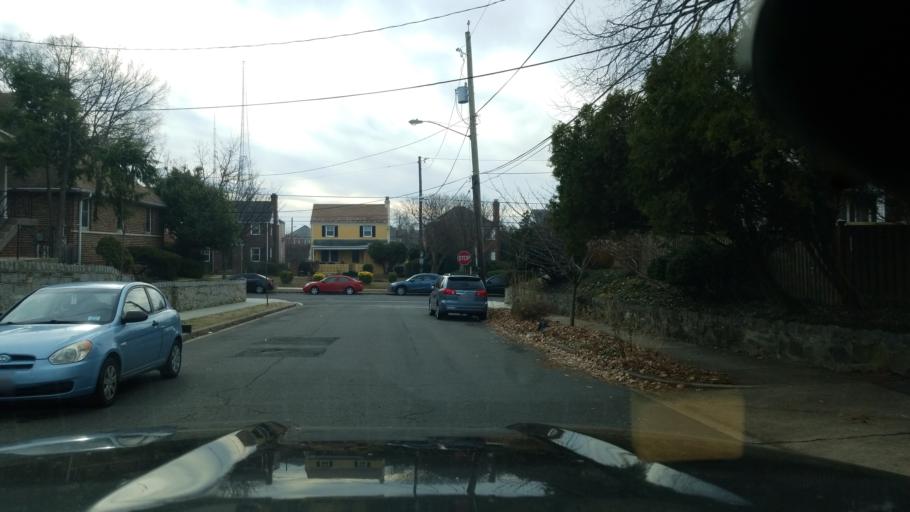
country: US
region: Maryland
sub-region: Montgomery County
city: Silver Spring
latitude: 38.9704
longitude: -77.0285
